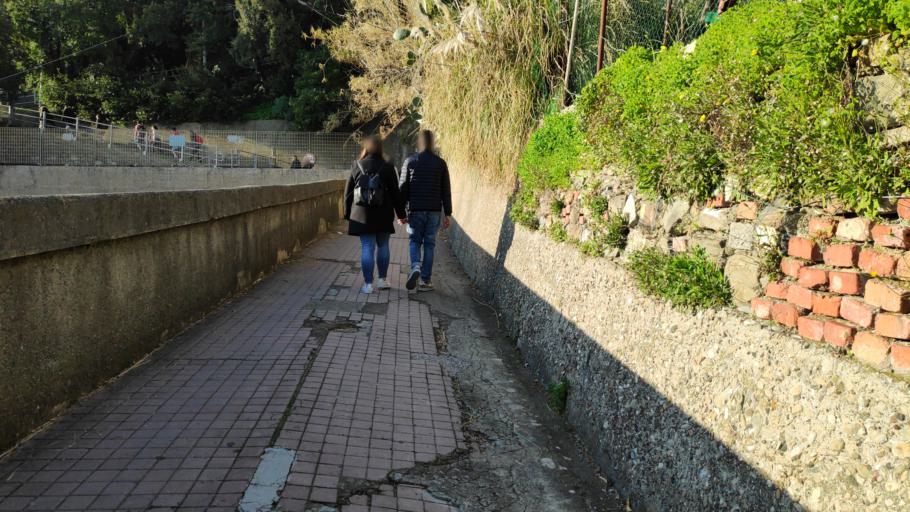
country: IT
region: Liguria
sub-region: Provincia di La Spezia
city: Vernazza
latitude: 44.1197
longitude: 9.7121
